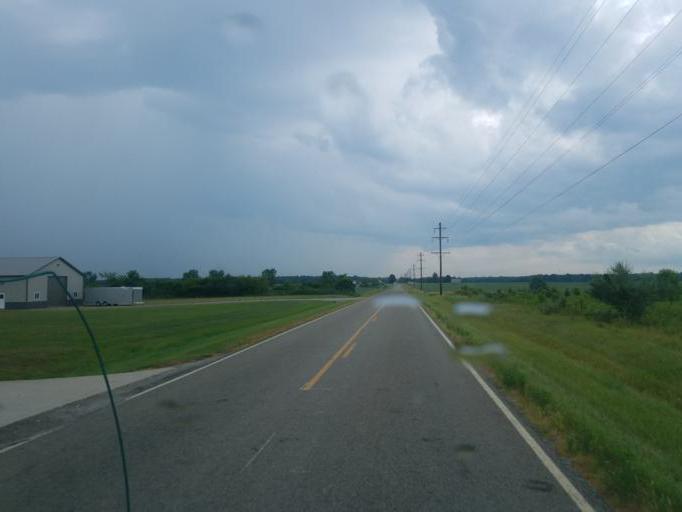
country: US
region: Ohio
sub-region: Williams County
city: Edgerton
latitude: 41.3745
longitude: -84.7670
